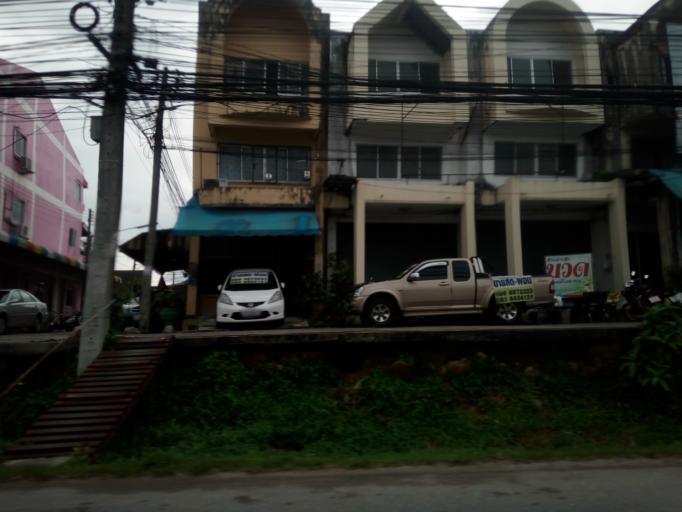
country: TH
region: Phuket
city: Thalang
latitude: 7.9834
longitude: 98.3613
